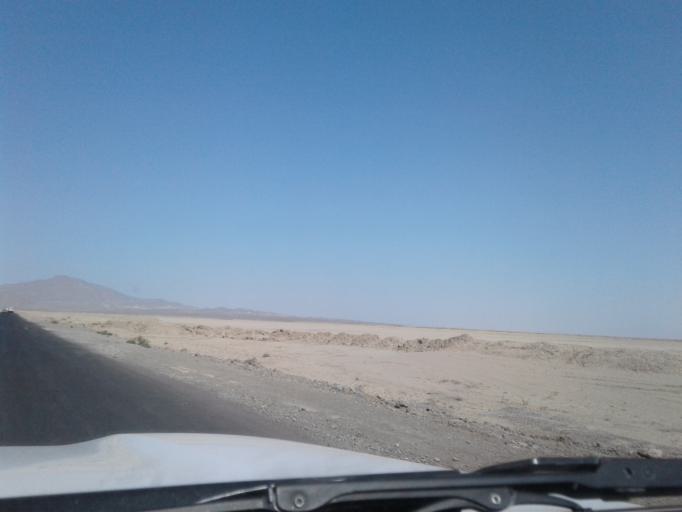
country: TM
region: Balkan
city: Gumdag
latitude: 39.2308
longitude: 54.6836
